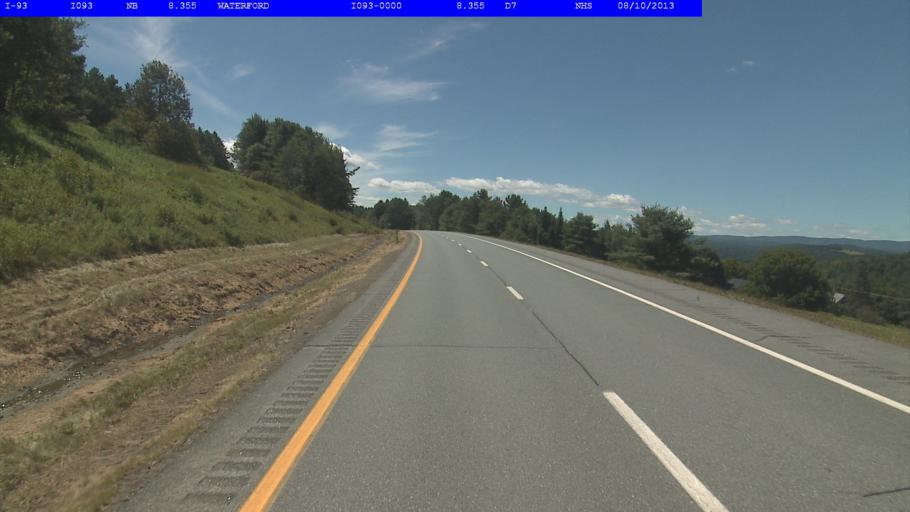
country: US
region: Vermont
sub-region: Caledonia County
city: Saint Johnsbury
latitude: 44.4205
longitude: -71.9701
